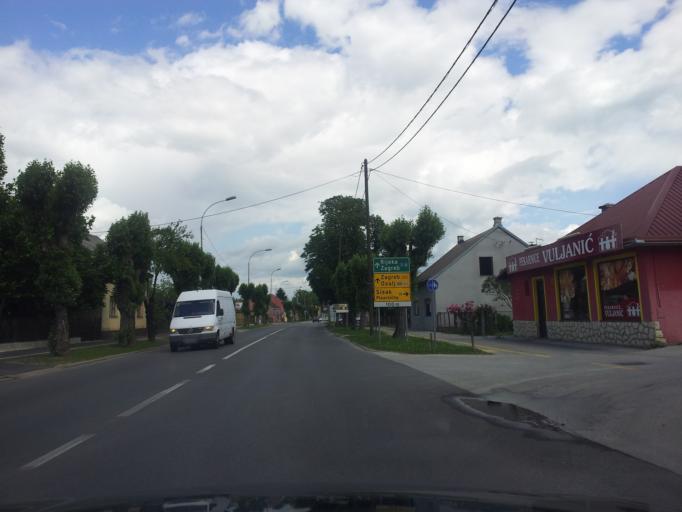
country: HR
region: Karlovacka
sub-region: Grad Karlovac
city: Karlovac
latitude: 45.5077
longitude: 15.5488
